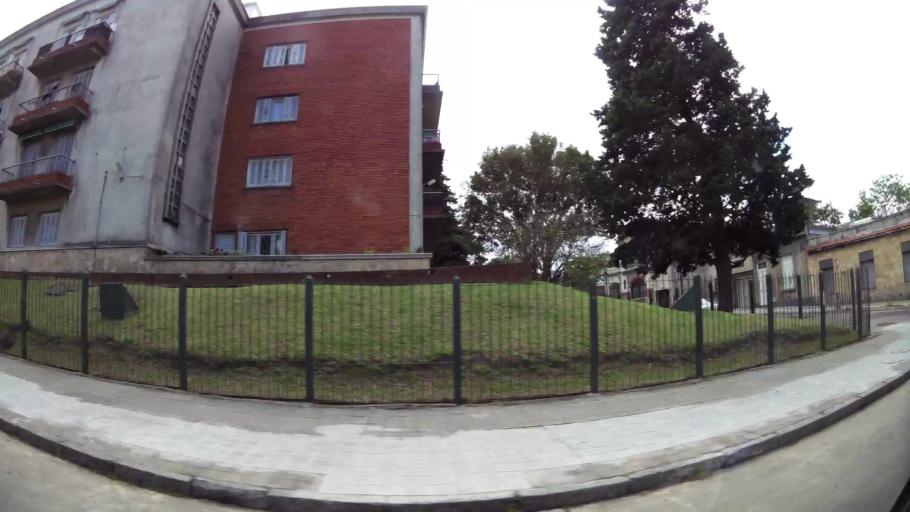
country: UY
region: Montevideo
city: Montevideo
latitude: -34.8789
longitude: -56.1439
